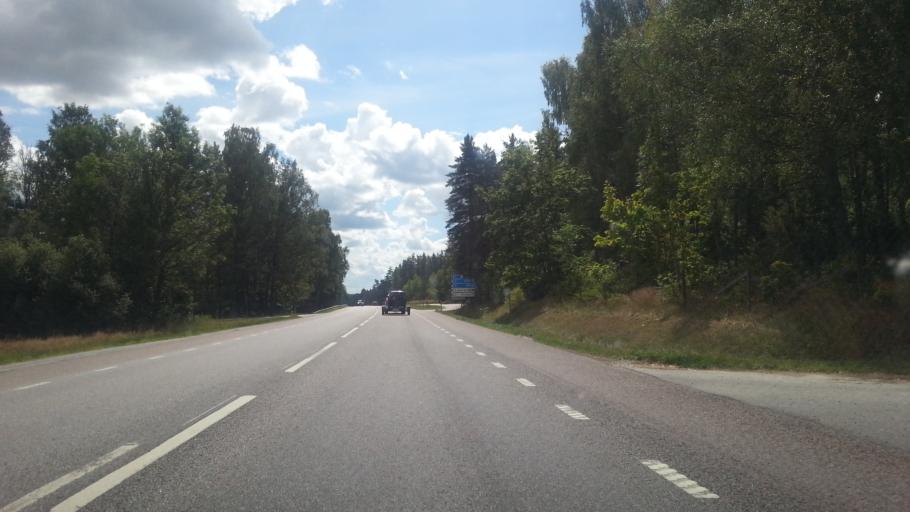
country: SE
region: OErebro
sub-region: Nora Kommun
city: Nora
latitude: 59.4497
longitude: 15.1372
